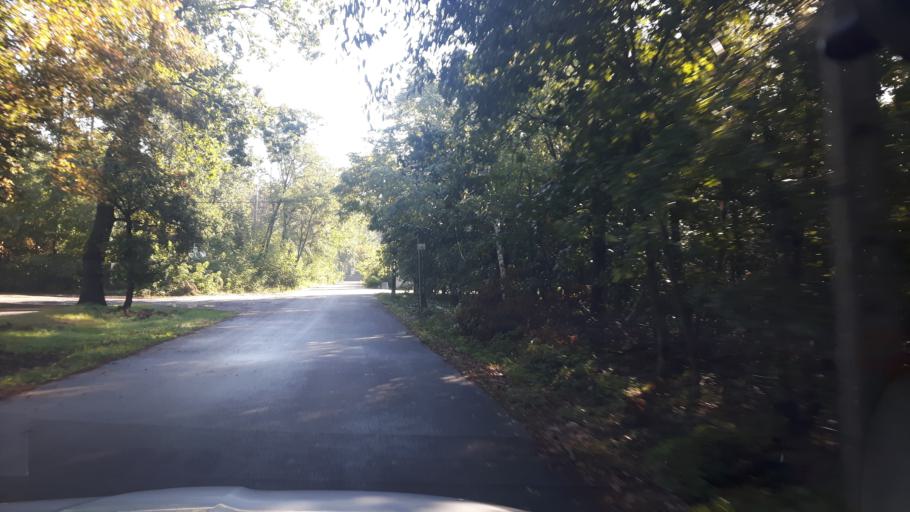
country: PL
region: Masovian Voivodeship
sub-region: Warszawa
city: Bialoleka
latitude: 52.3589
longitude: 20.9750
